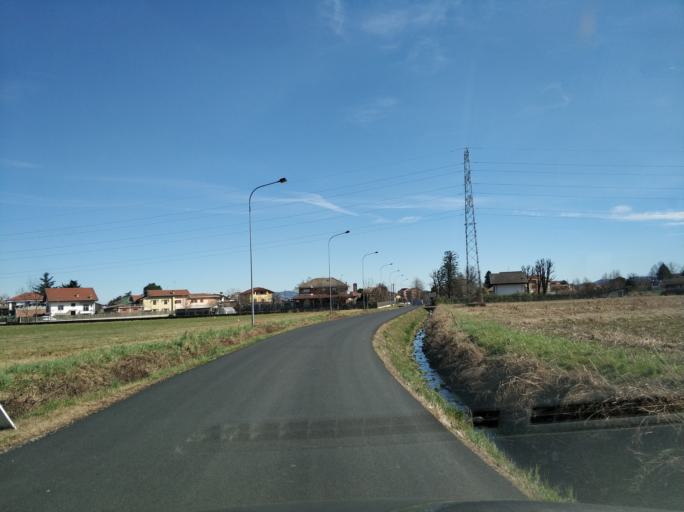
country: IT
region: Piedmont
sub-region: Provincia di Torino
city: Leini
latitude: 45.1881
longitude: 7.7040
